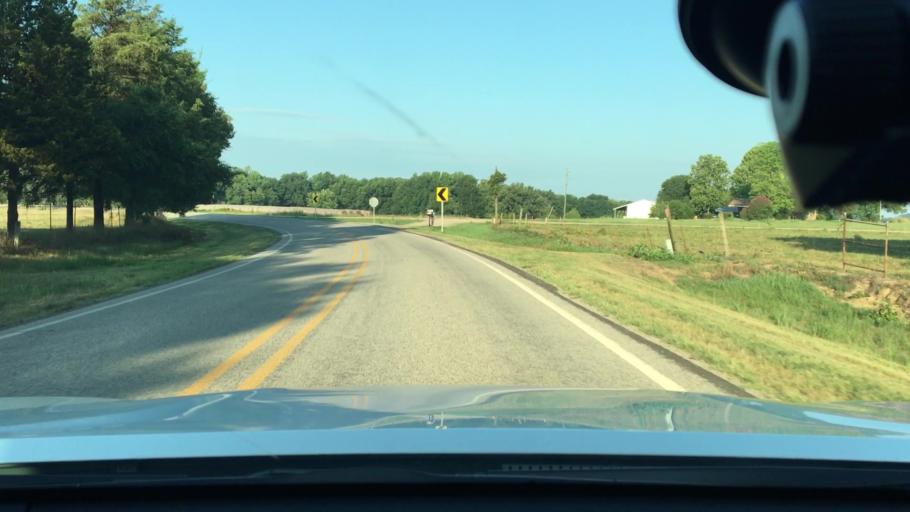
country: US
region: Arkansas
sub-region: Johnson County
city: Coal Hill
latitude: 35.3556
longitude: -93.5650
